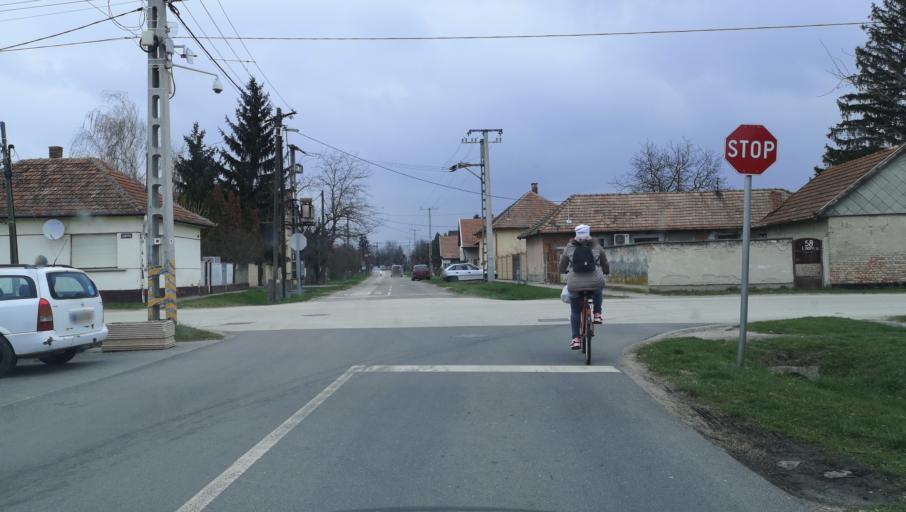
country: HU
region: Pest
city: Monor
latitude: 47.3540
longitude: 19.4498
